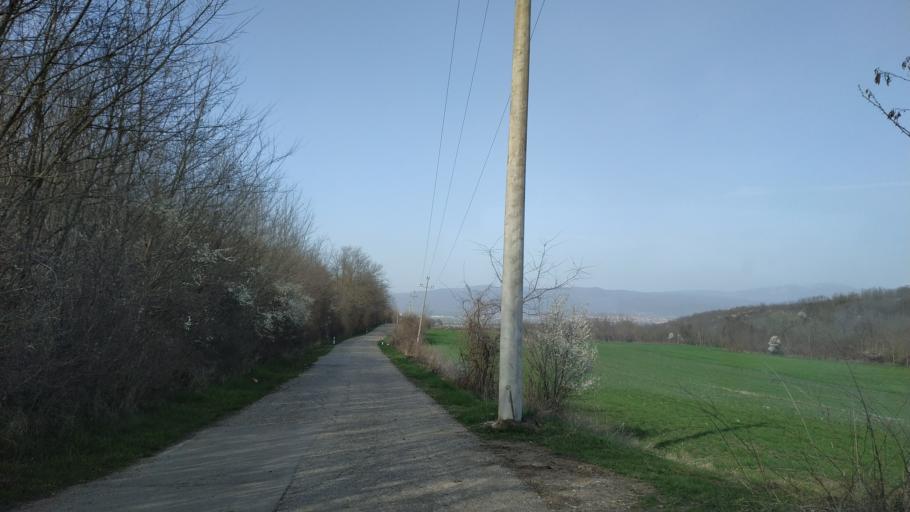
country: RS
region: Central Serbia
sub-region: Nisavski Okrug
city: Aleksinac
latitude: 43.5083
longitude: 21.6448
